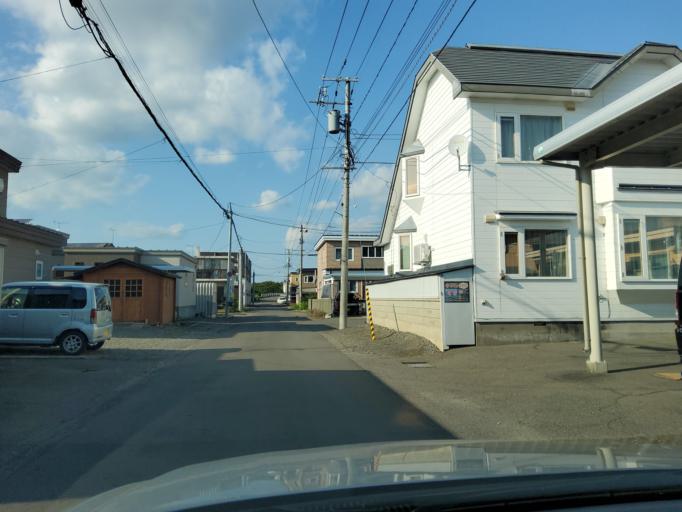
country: JP
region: Hokkaido
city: Obihiro
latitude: 42.8935
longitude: 143.1978
